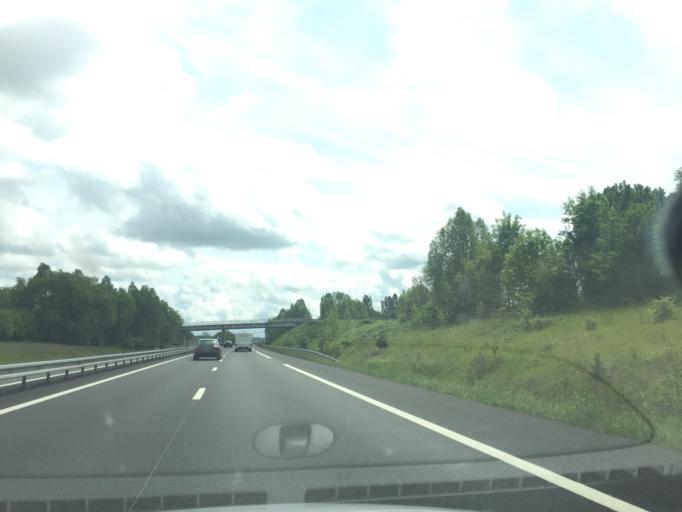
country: FR
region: Pays de la Loire
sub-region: Departement de la Sarthe
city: Teloche
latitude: 47.8916
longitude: 0.3053
